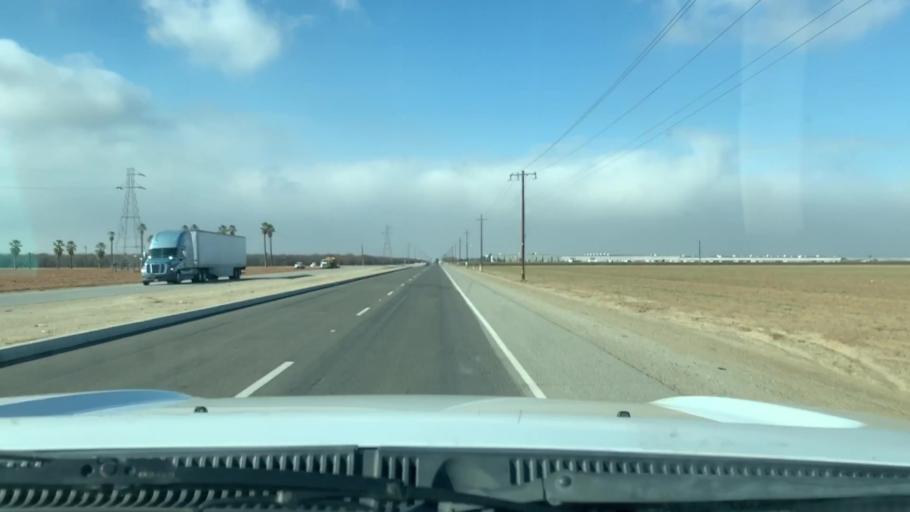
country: US
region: California
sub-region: Kern County
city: Rosedale
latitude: 35.4417
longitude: -119.1682
